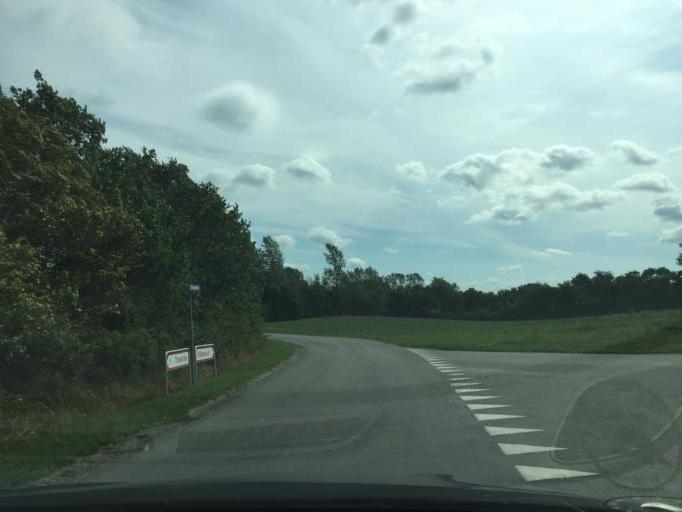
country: DK
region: South Denmark
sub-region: Assens Kommune
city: Tommerup
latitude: 55.3953
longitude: 10.2447
